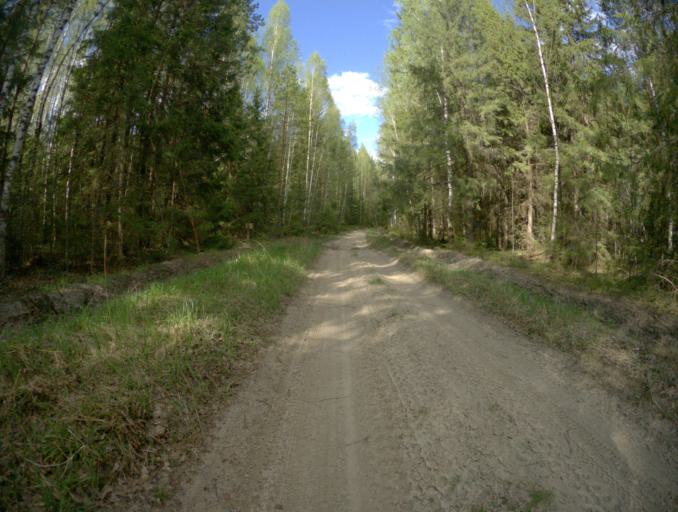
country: RU
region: Vladimir
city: Golovino
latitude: 55.8909
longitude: 40.4093
